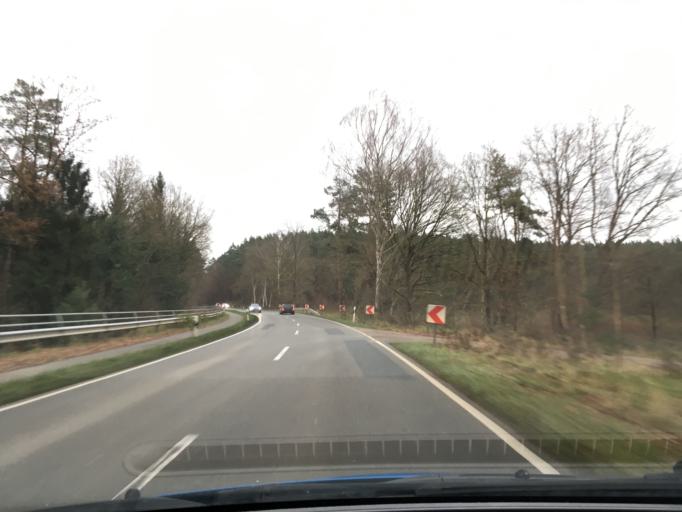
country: DE
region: Lower Saxony
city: Neetze
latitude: 53.2660
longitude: 10.6522
